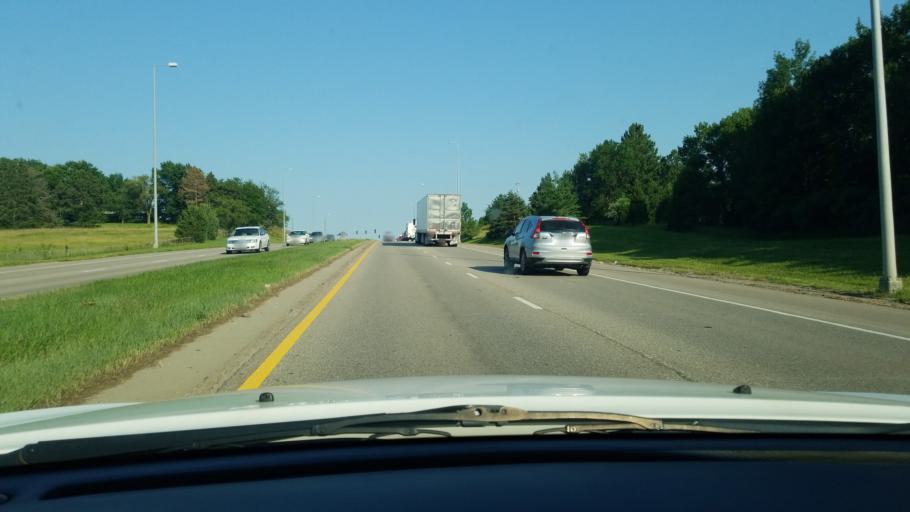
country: US
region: Nebraska
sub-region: Lancaster County
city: Lincoln
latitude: 40.7477
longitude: -96.6283
